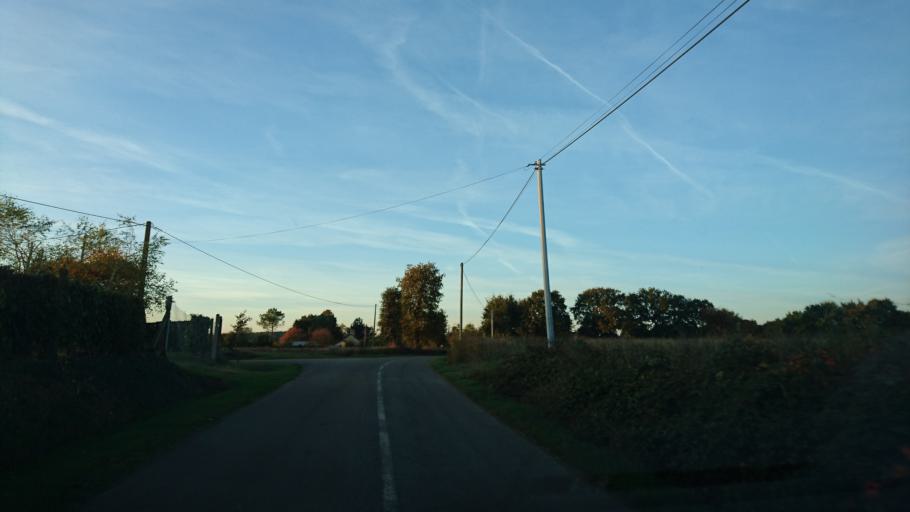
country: FR
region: Brittany
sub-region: Departement d'Ille-et-Vilaine
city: Bruz
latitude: 48.0024
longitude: -1.7535
